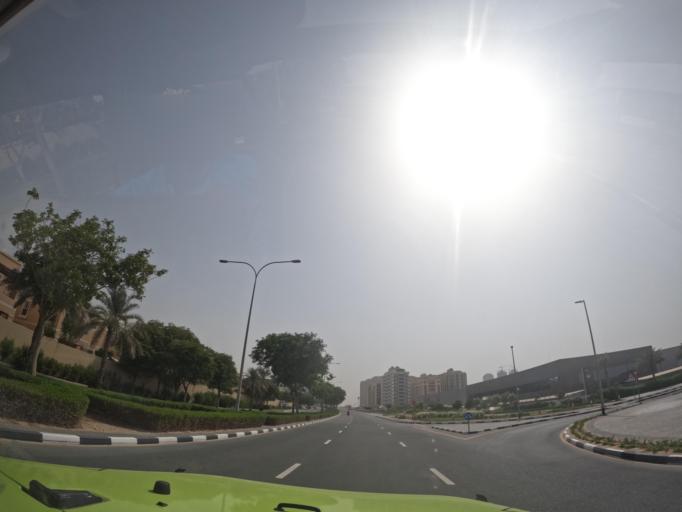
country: AE
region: Dubai
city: Dubai
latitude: 25.1171
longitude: 55.3821
